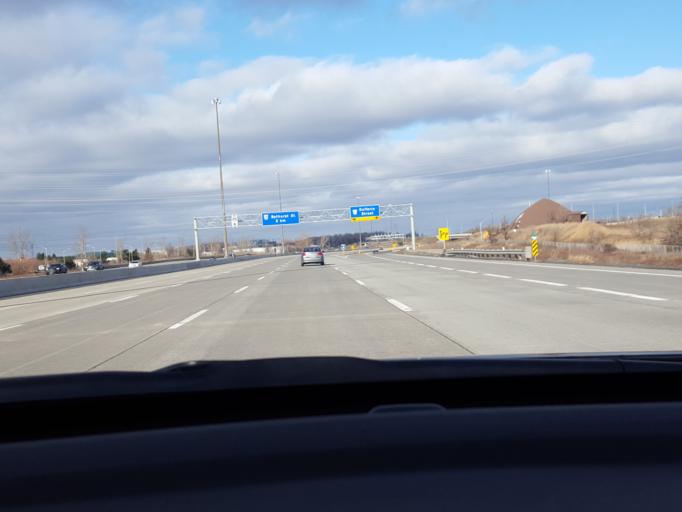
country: CA
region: Ontario
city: Concord
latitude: 43.8097
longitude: -79.4797
